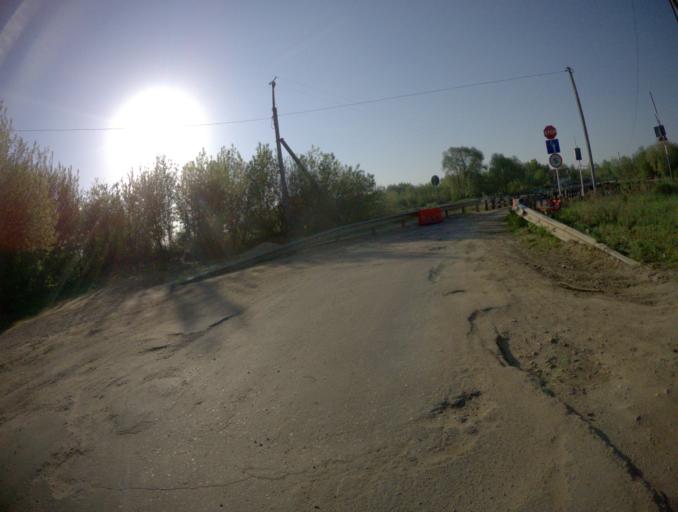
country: RU
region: Vladimir
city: Vyazniki
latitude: 56.2556
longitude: 42.1784
